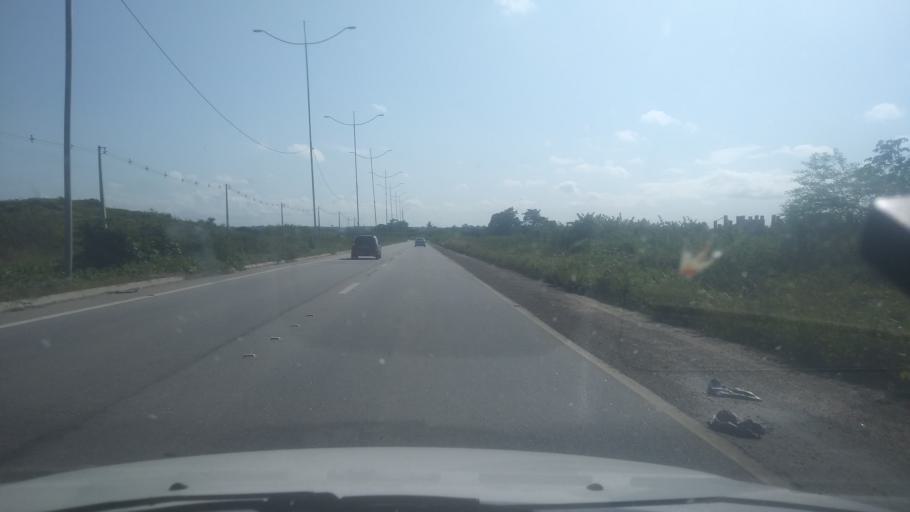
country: BR
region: Rio Grande do Norte
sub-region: Macaiba
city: Macaiba
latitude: -5.8177
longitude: -35.3643
